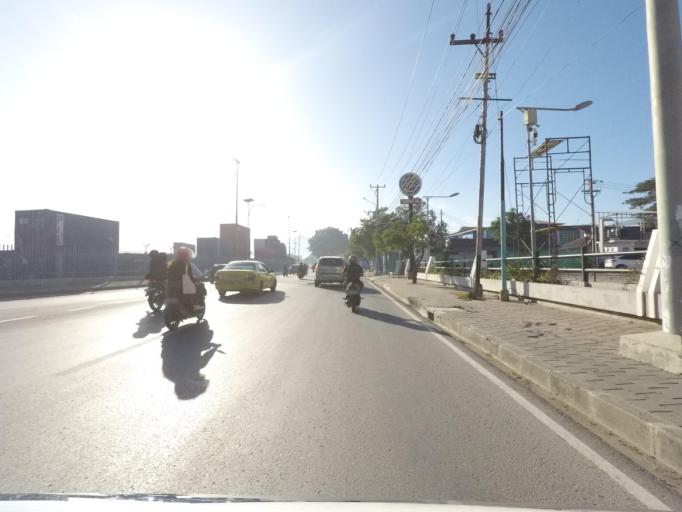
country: TL
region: Dili
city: Dili
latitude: -8.5540
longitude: 125.5745
